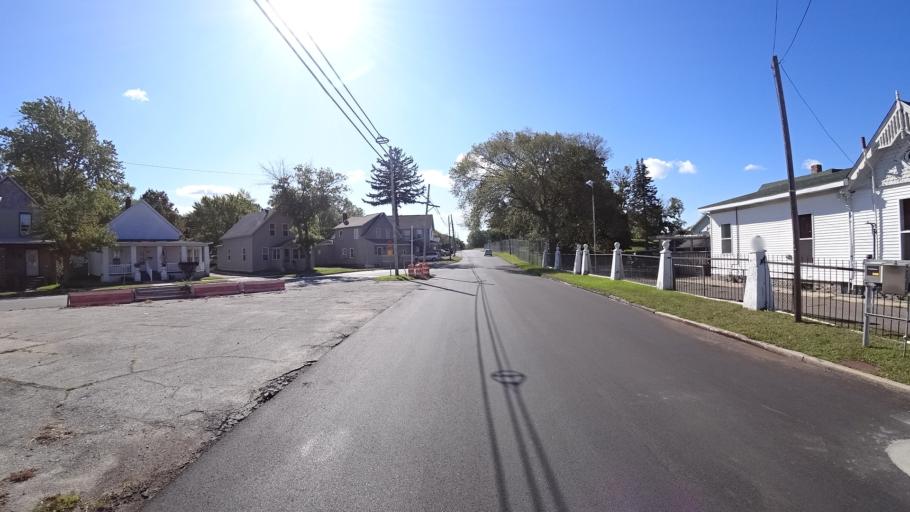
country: US
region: Indiana
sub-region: LaPorte County
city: Michigan City
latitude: 41.7033
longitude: -86.9140
